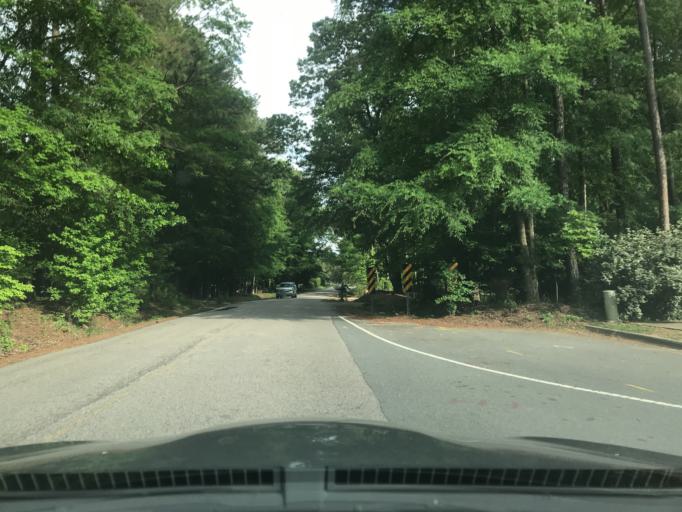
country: US
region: North Carolina
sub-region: Wake County
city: Wake Forest
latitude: 35.9234
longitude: -78.5742
